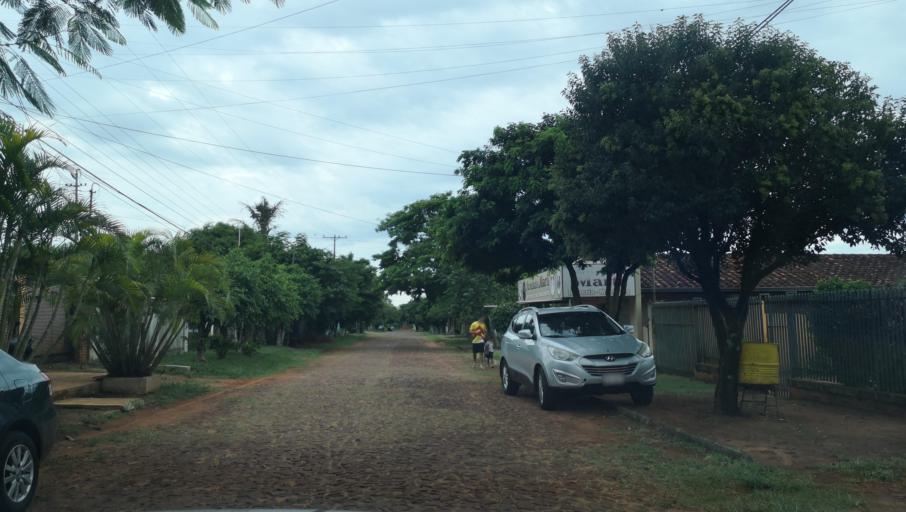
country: PY
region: Misiones
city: Santa Maria
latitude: -26.8872
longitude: -57.0394
